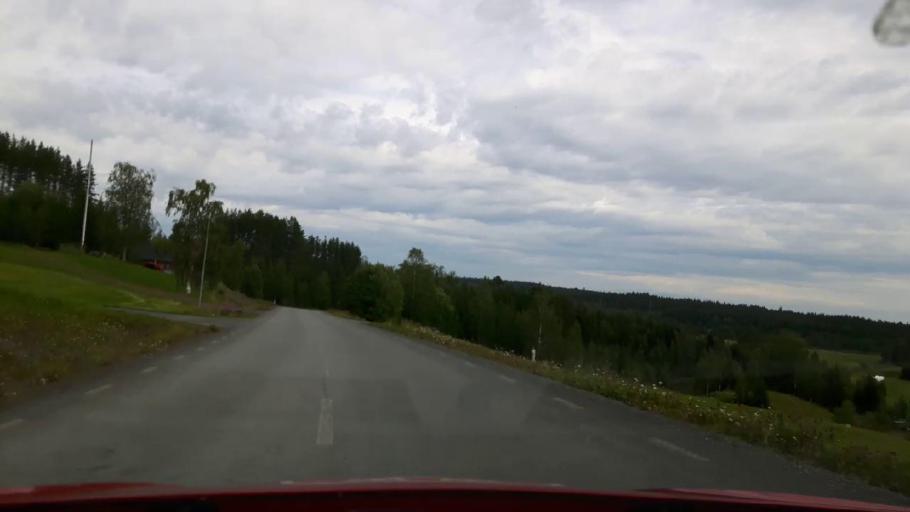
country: SE
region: Jaemtland
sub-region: OEstersunds Kommun
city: Lit
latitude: 63.4253
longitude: 15.2591
